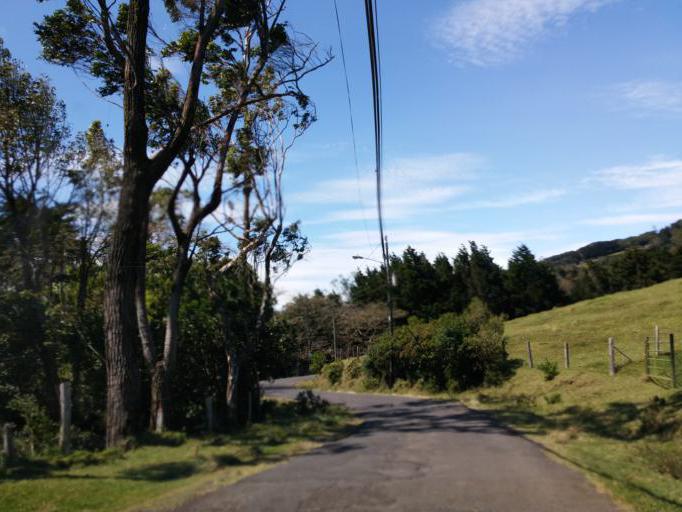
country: CR
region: Heredia
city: Santo Domingo
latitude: 10.0950
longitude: -84.1140
